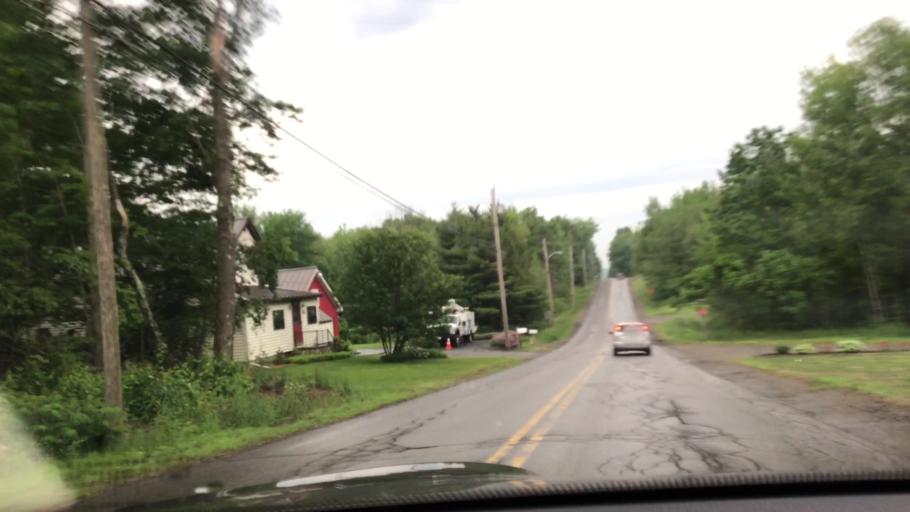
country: US
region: Maine
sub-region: Penobscot County
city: Orono
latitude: 44.8946
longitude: -68.6998
